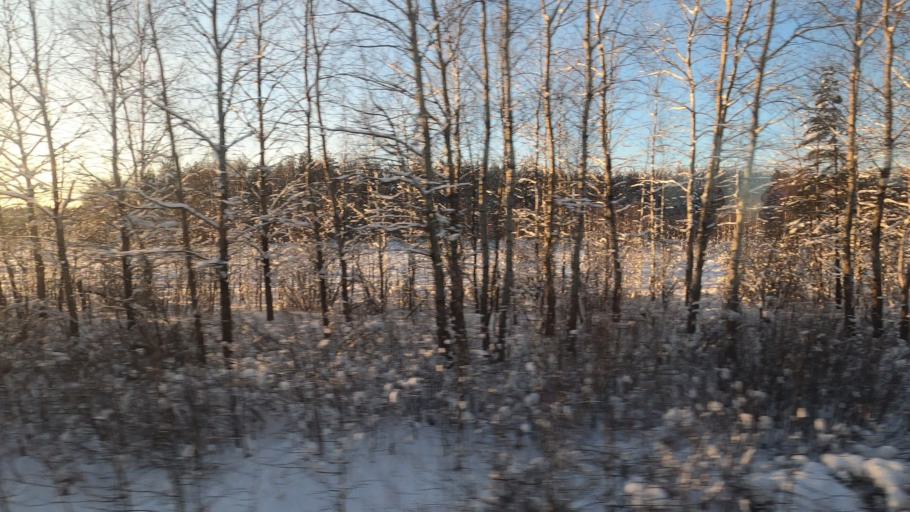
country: RU
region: Moskovskaya
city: Taldom
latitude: 56.6516
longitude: 37.5653
